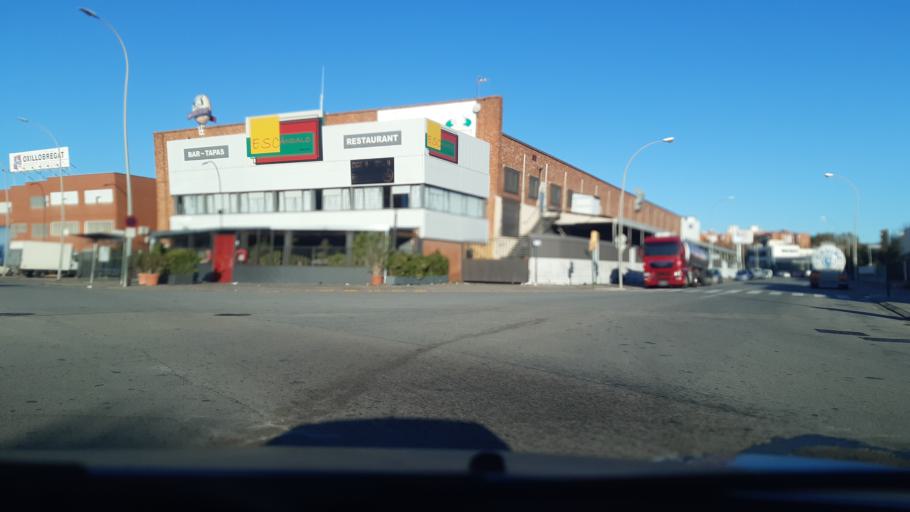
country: ES
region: Catalonia
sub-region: Provincia de Barcelona
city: Sant Boi de Llobregat
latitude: 41.3351
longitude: 2.0484
